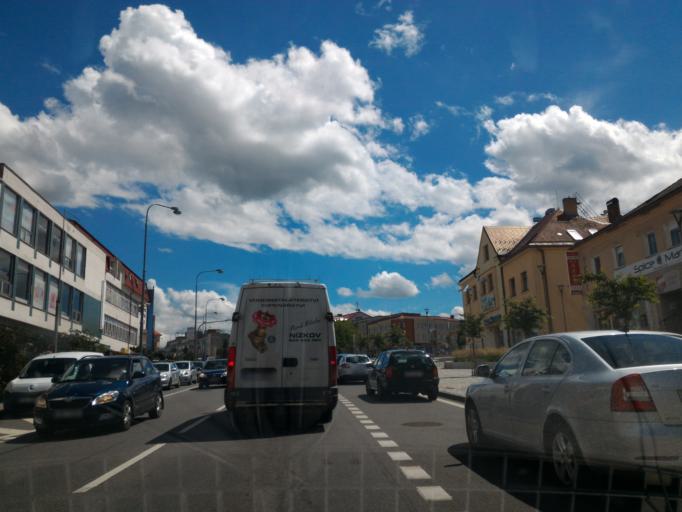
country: CZ
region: Vysocina
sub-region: Okres Zd'ar nad Sazavou
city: Zd'ar nad Sazavou
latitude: 49.5635
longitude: 15.9397
